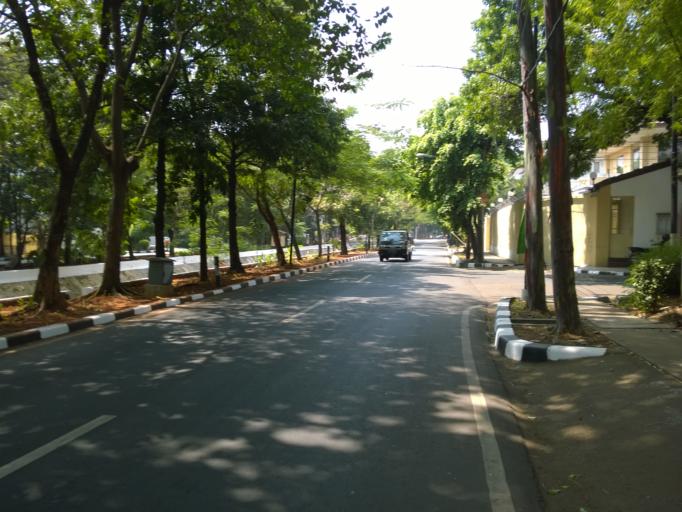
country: ID
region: Jakarta Raya
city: Jakarta
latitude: -6.1959
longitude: 106.8319
